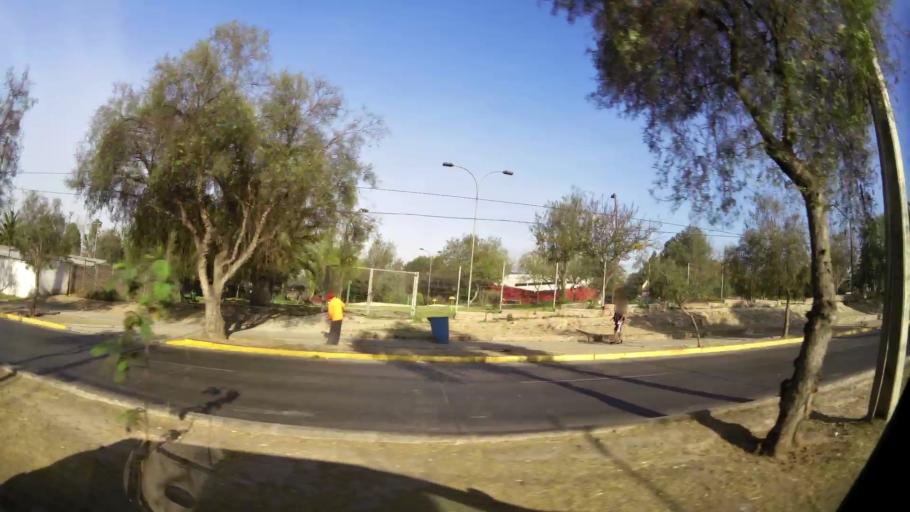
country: CL
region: Santiago Metropolitan
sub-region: Provincia de Santiago
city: Lo Prado
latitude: -33.4469
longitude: -70.7396
